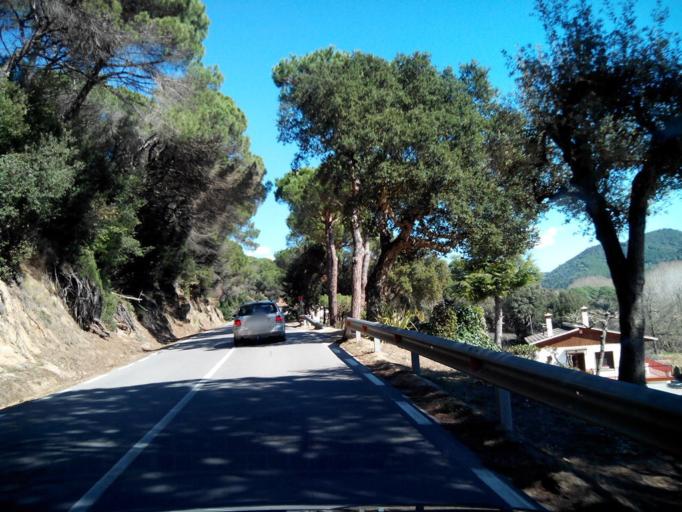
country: ES
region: Catalonia
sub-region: Provincia de Barcelona
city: Dosrius
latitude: 41.5942
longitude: 2.4337
